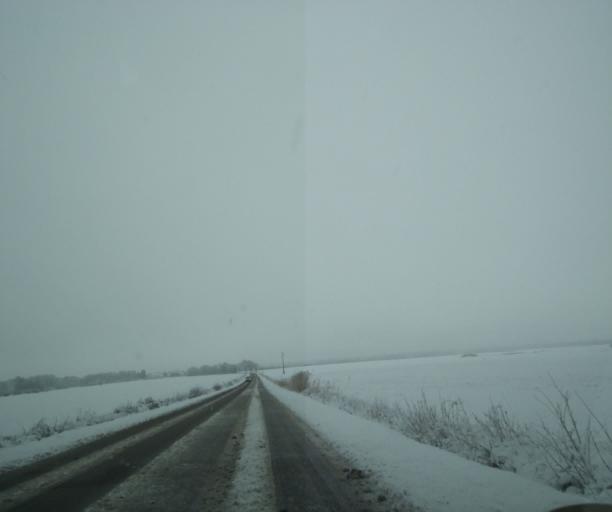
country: FR
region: Champagne-Ardenne
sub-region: Departement de la Haute-Marne
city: Saint-Dizier
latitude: 48.5954
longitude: 4.9059
